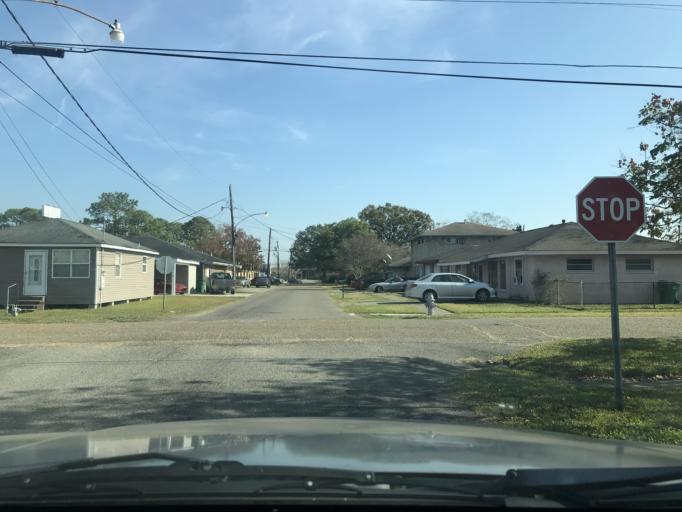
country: US
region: Louisiana
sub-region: Jefferson Parish
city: Marrero
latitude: 29.8943
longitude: -90.0914
